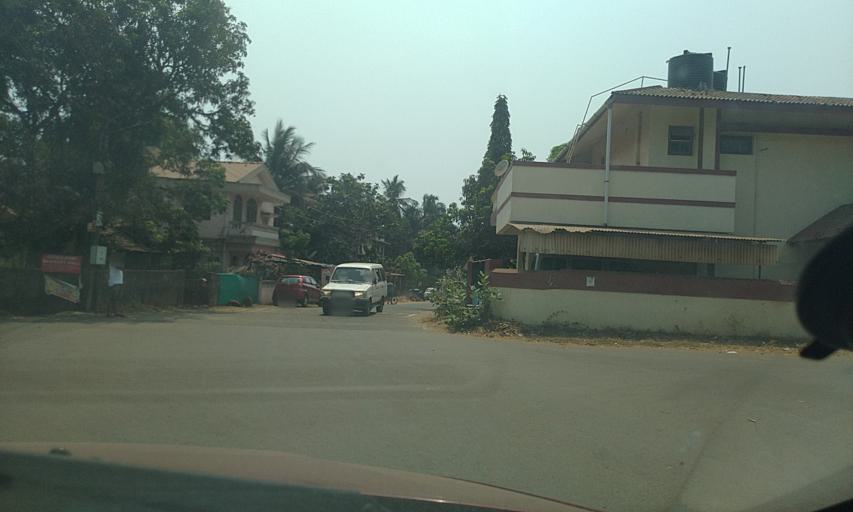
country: IN
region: Goa
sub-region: North Goa
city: Serula
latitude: 15.5235
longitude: 73.8331
